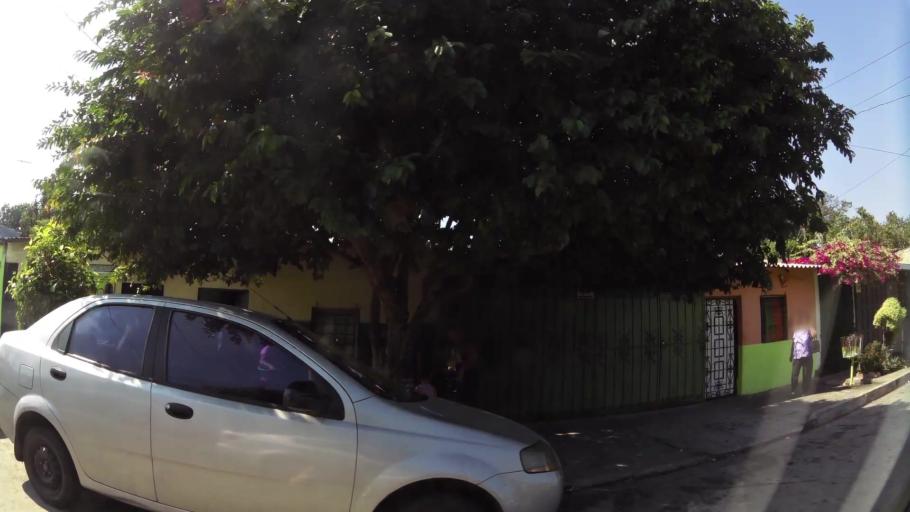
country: SV
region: La Libertad
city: Antiguo Cuscatlan
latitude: 13.6733
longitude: -89.2406
